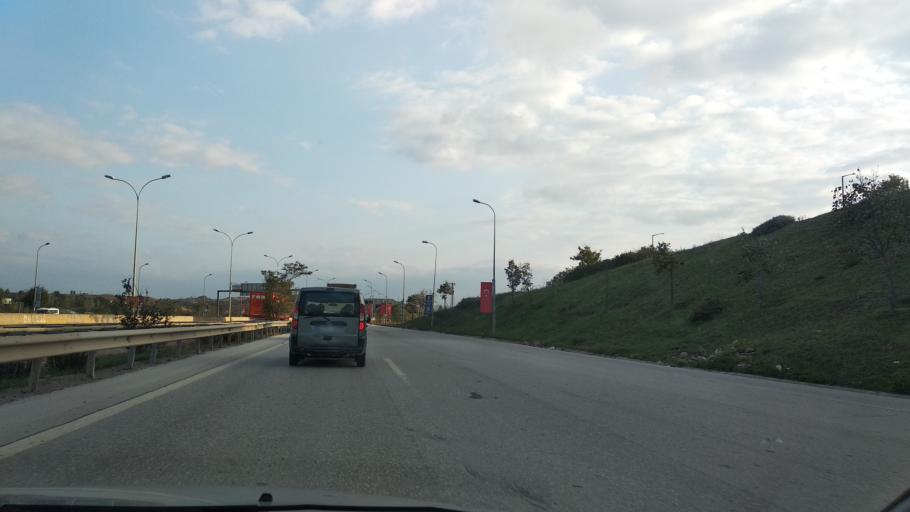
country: TR
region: Istanbul
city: Pendik
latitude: 40.9123
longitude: 29.3257
